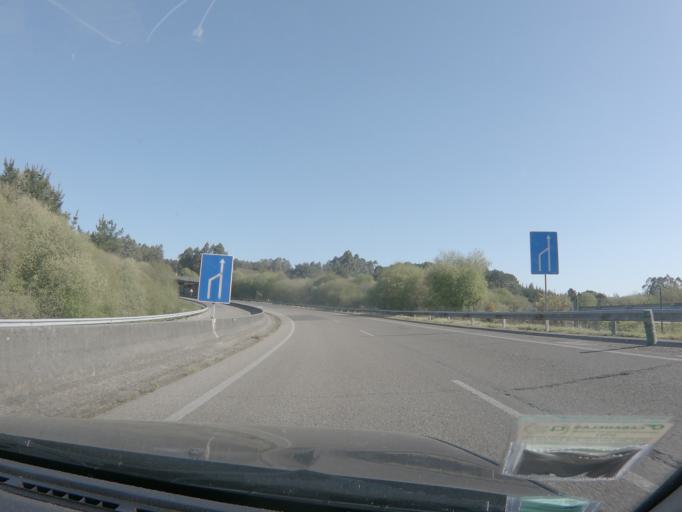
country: ES
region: Galicia
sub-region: Provincia da Coruna
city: Betanzos
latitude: 43.2663
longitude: -8.2440
